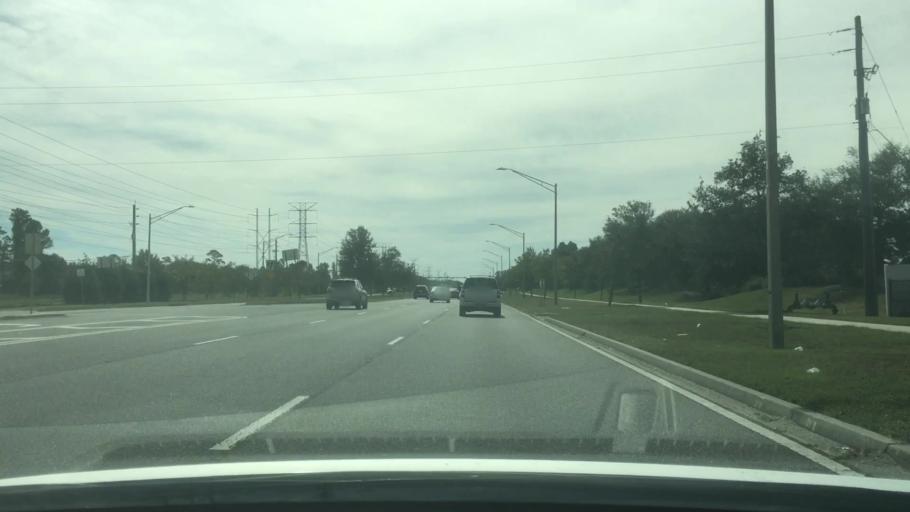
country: US
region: Florida
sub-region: Duval County
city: Atlantic Beach
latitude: 30.3156
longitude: -81.4894
